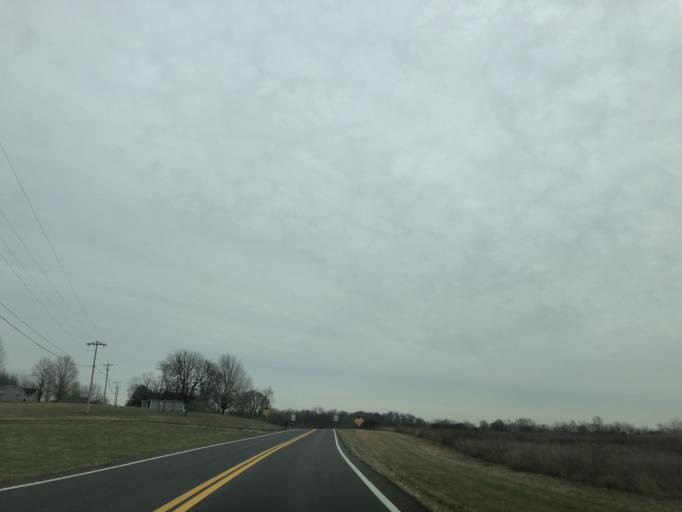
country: US
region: Tennessee
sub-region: Sumner County
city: White House
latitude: 36.4759
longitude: -86.7182
